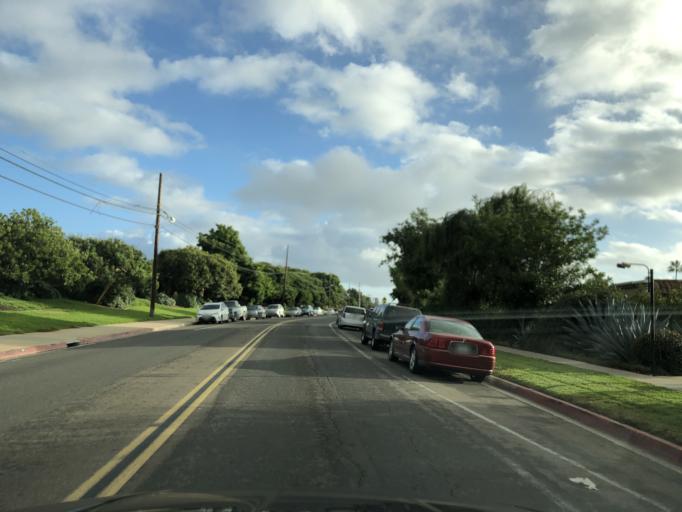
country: US
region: California
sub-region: San Diego County
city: La Jolla
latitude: 32.8160
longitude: -117.1826
